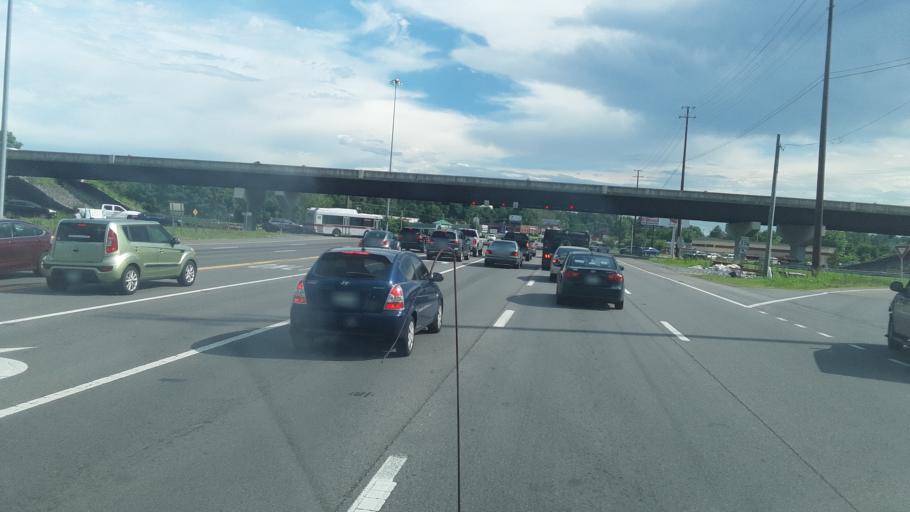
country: US
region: Tennessee
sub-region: Montgomery County
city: Clarksville
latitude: 36.5735
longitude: -87.3030
